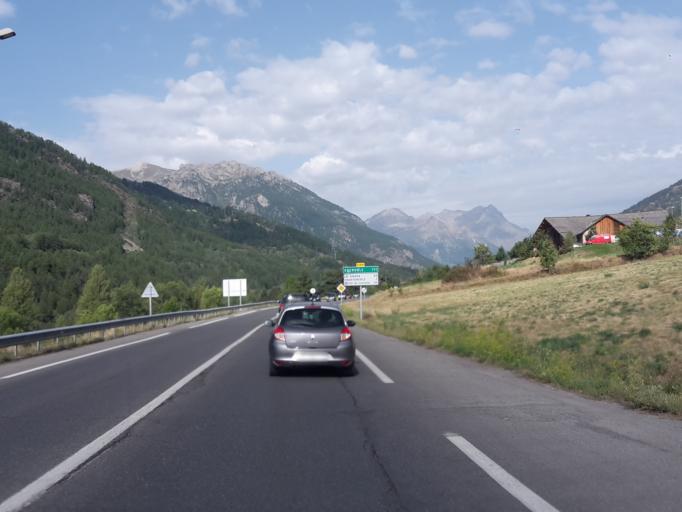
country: FR
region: Provence-Alpes-Cote d'Azur
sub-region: Departement des Hautes-Alpes
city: Saint-Chaffrey
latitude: 44.9226
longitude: 6.6113
